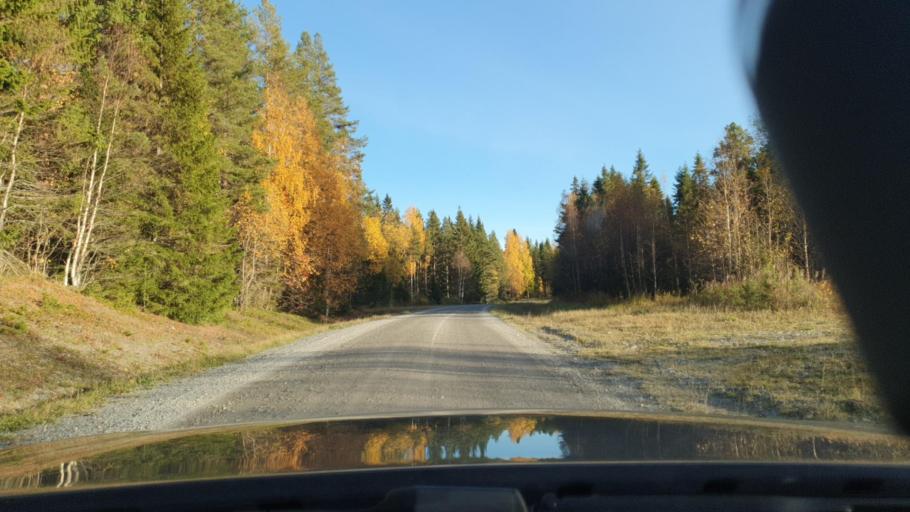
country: SE
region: Jaemtland
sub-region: Stroemsunds Kommun
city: Stroemsund
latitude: 63.5304
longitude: 15.6209
